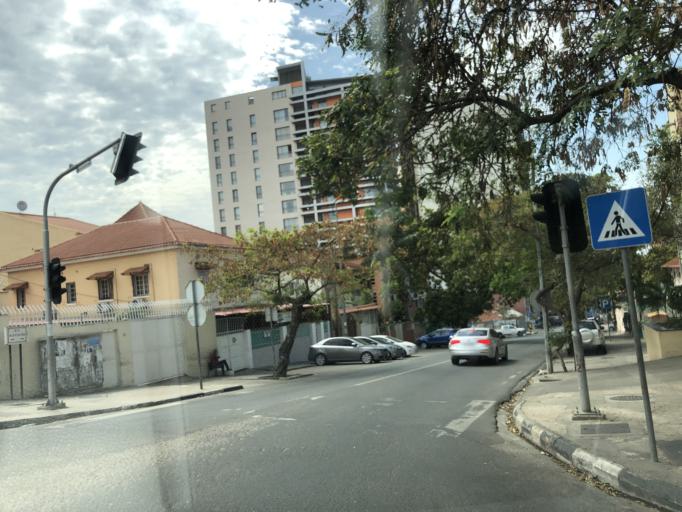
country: AO
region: Luanda
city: Luanda
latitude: -8.8205
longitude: 13.2328
